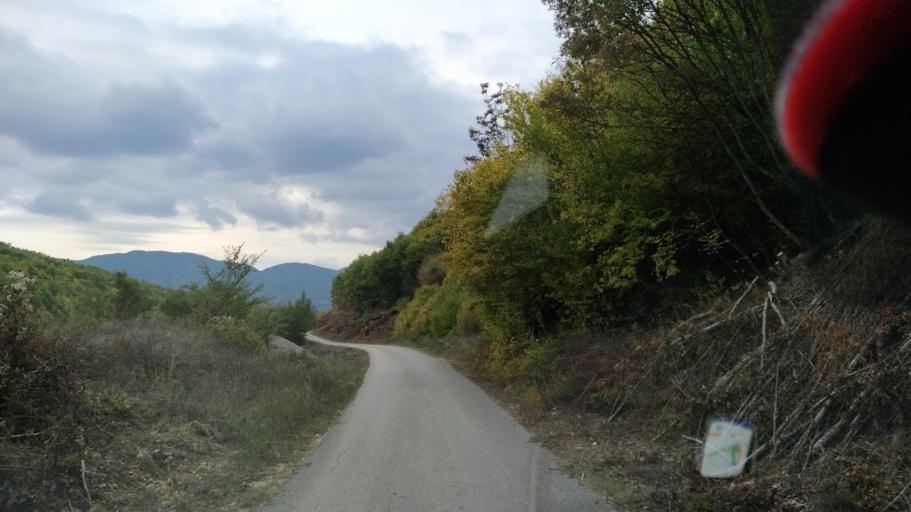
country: MK
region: Konce
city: Konce
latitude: 41.5088
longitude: 22.4773
